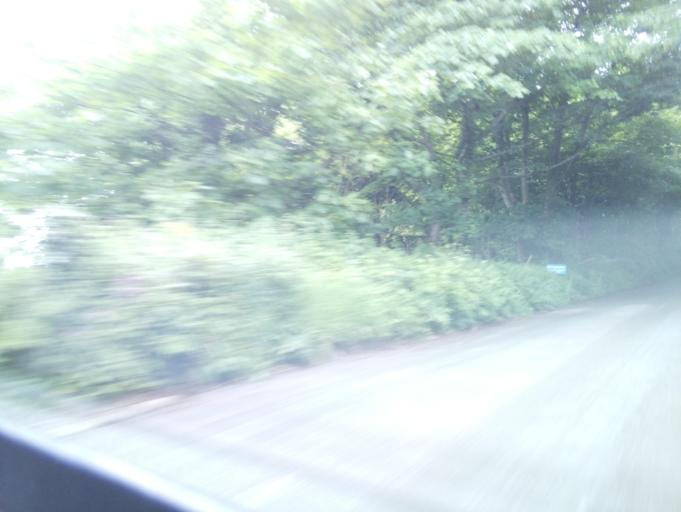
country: GB
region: England
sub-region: Devon
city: Dartmouth
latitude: 50.3566
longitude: -3.5443
